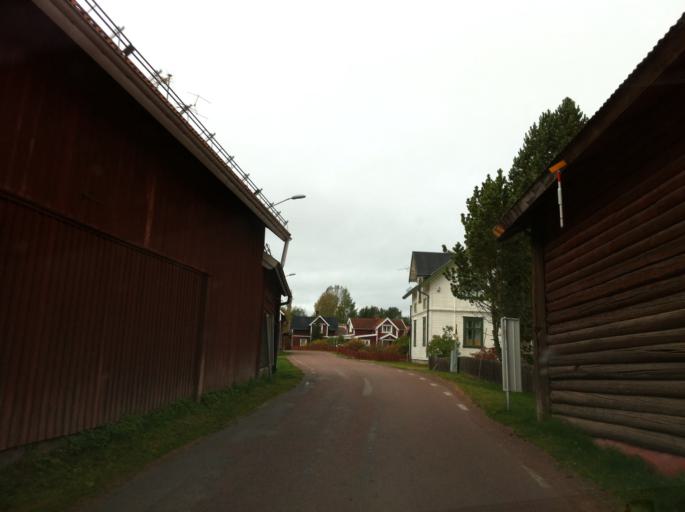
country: SE
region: Dalarna
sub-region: Mora Kommun
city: Mora
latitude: 61.1170
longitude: 14.4721
